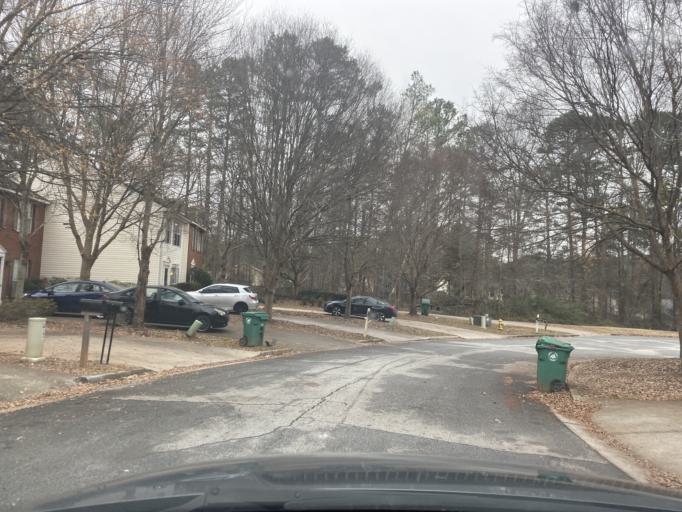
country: US
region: Georgia
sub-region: DeKalb County
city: Pine Mountain
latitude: 33.6954
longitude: -84.1615
